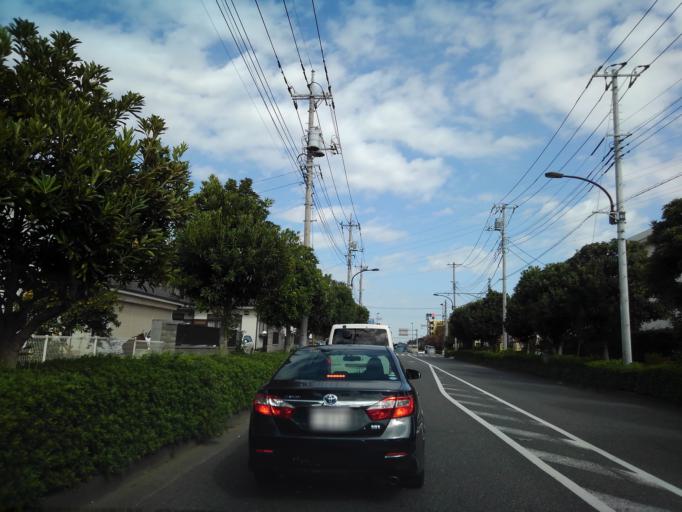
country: JP
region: Tokyo
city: Tanashicho
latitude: 35.7299
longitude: 139.4984
